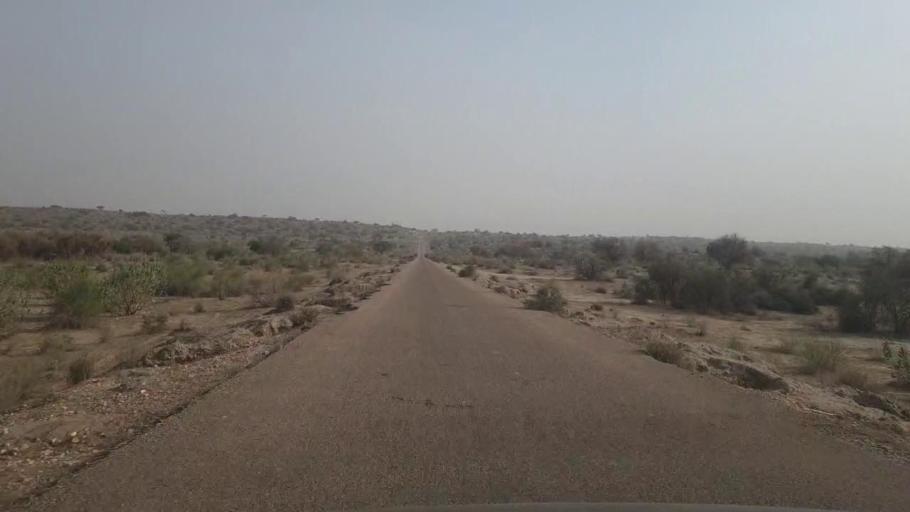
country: PK
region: Sindh
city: Chor
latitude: 25.4910
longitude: 69.9715
